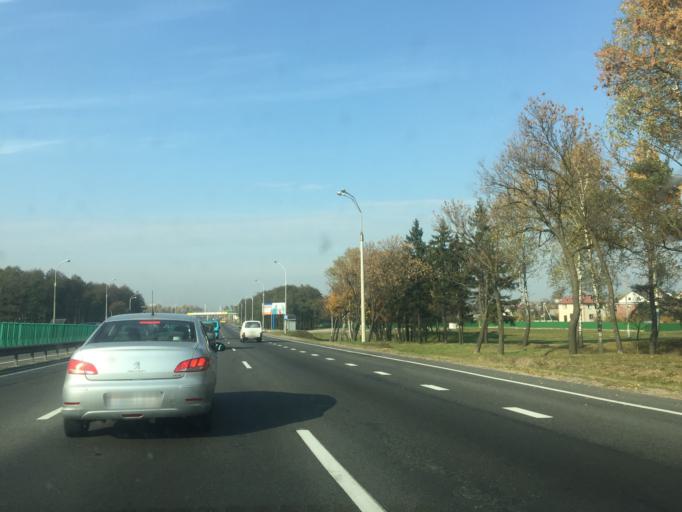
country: BY
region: Minsk
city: Vyaliki Trastsyanets
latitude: 53.8428
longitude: 27.7168
